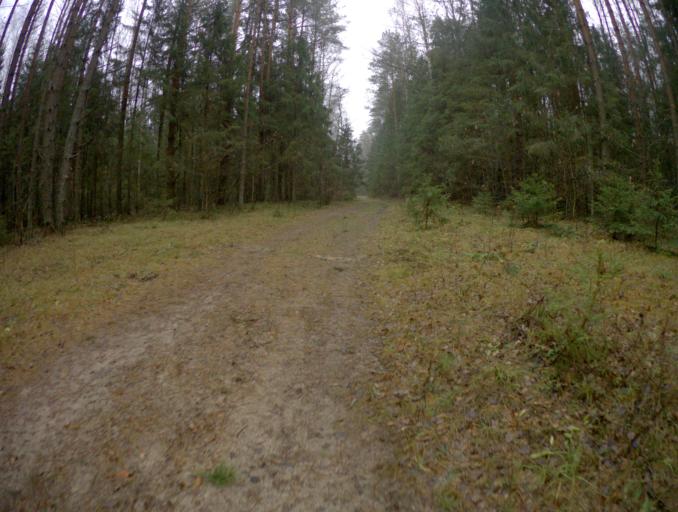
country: RU
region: Vladimir
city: Golovino
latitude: 56.0113
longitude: 40.4839
